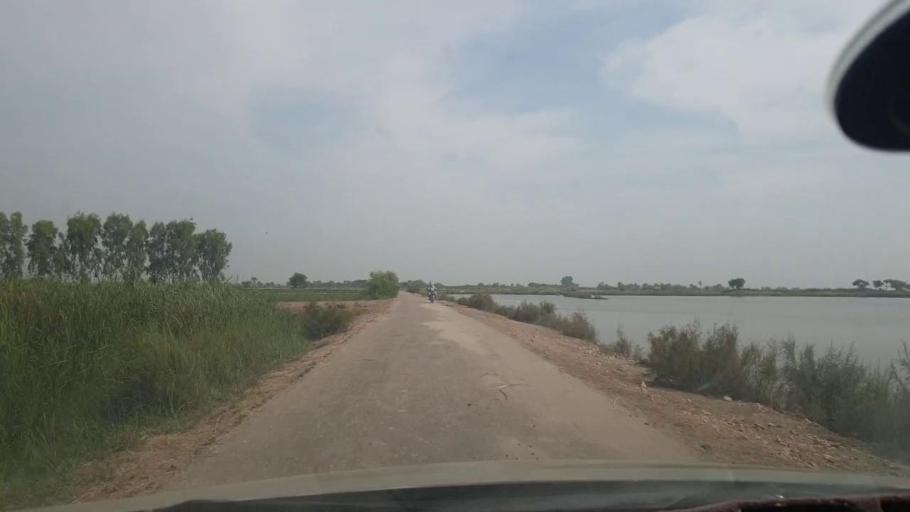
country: PK
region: Sindh
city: Jacobabad
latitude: 28.3085
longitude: 68.4763
